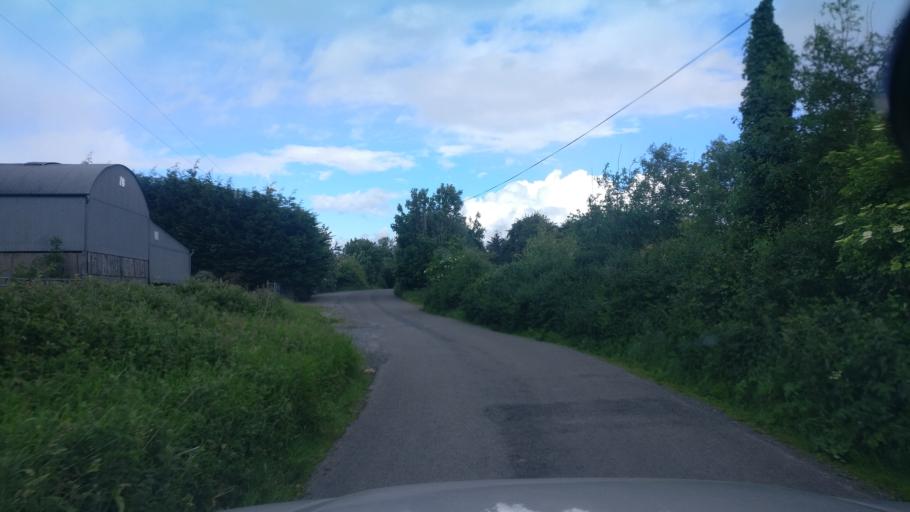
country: IE
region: Connaught
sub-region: County Galway
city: Portumna
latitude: 53.1989
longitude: -8.3245
